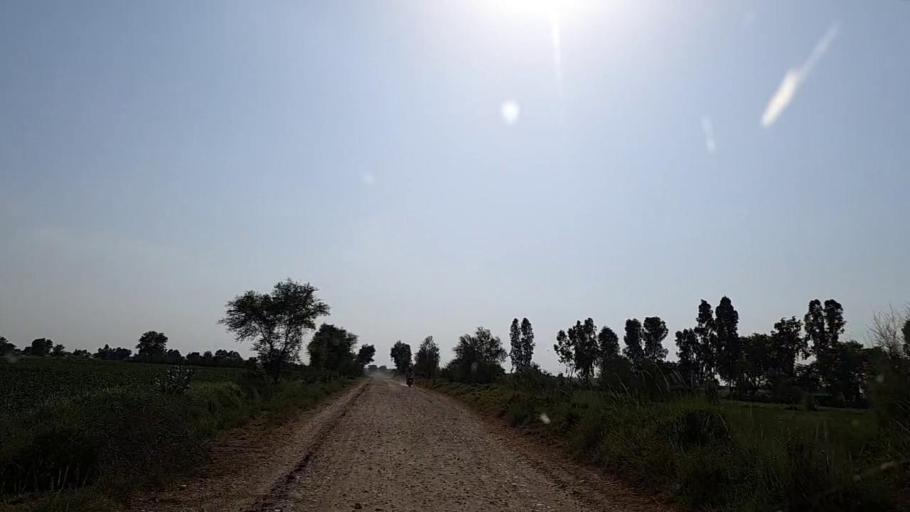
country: PK
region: Sindh
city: Khanpur
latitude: 27.7370
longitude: 69.3694
